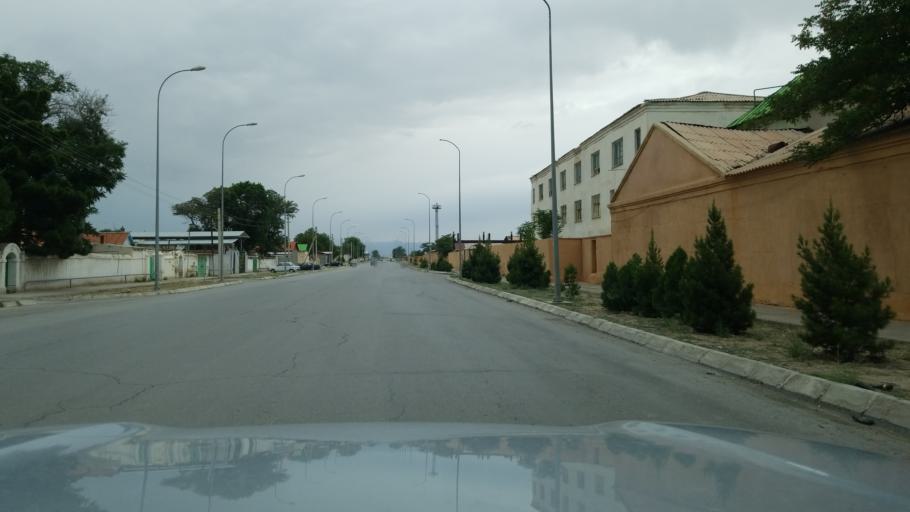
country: TM
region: Balkan
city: Serdar
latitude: 38.9773
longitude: 56.2721
